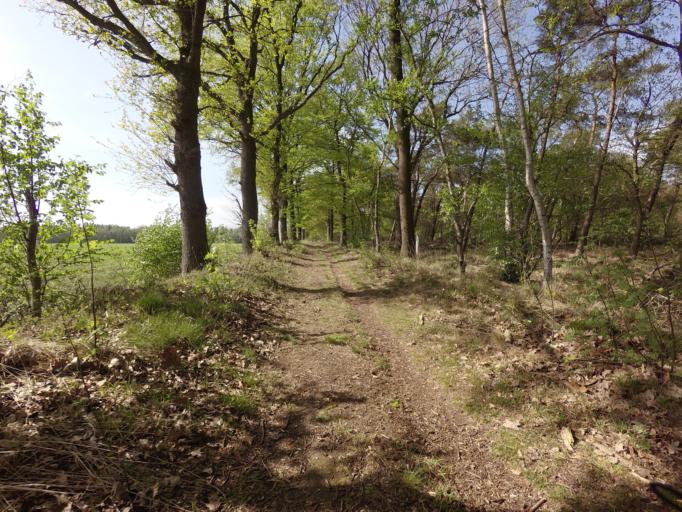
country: NL
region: North Brabant
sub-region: Gemeente Goirle
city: Goirle
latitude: 51.4776
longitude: 5.0023
